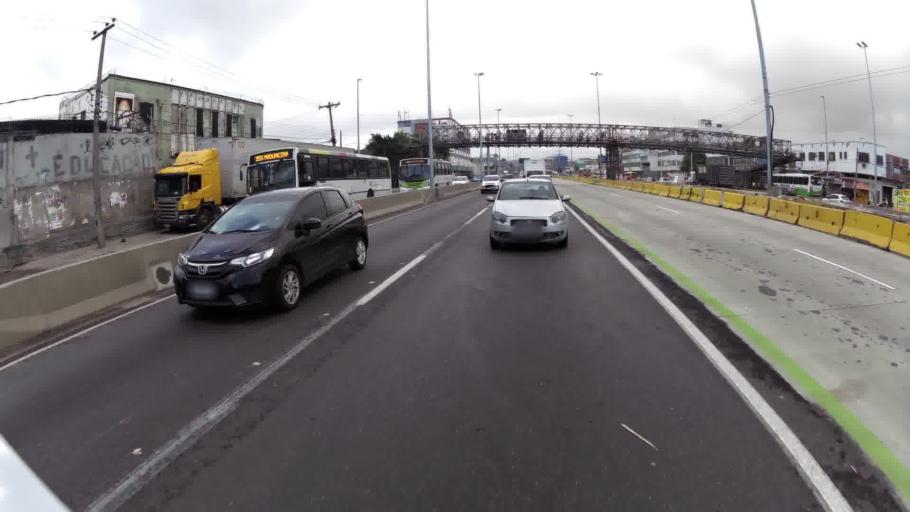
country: BR
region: Rio de Janeiro
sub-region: Rio De Janeiro
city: Rio de Janeiro
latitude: -22.8601
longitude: -43.2477
